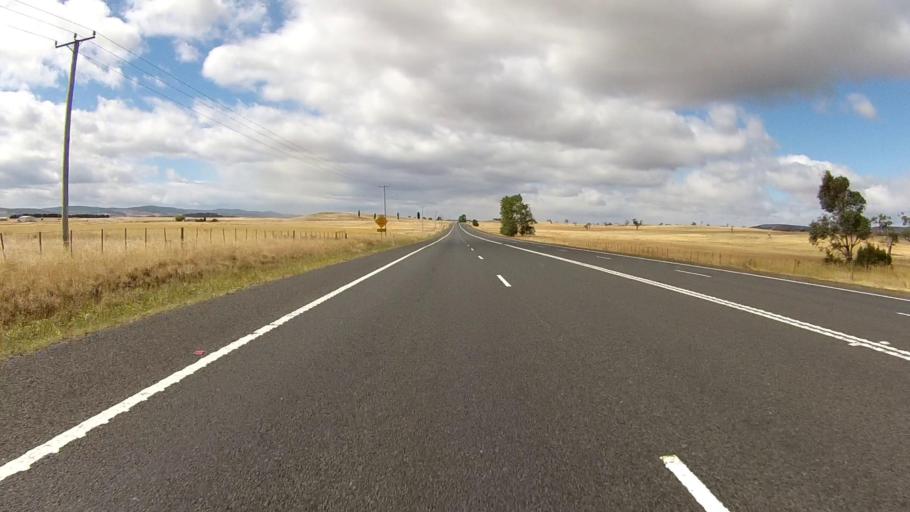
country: AU
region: Tasmania
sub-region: Northern Midlands
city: Evandale
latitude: -41.8714
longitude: 147.4605
